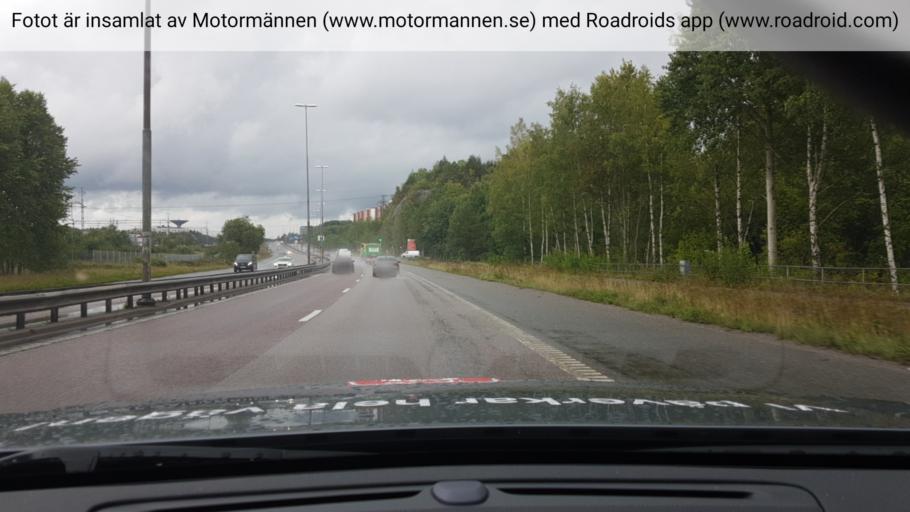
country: SE
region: Stockholm
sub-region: Huddinge Kommun
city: Huddinge
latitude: 59.2273
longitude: 17.9589
